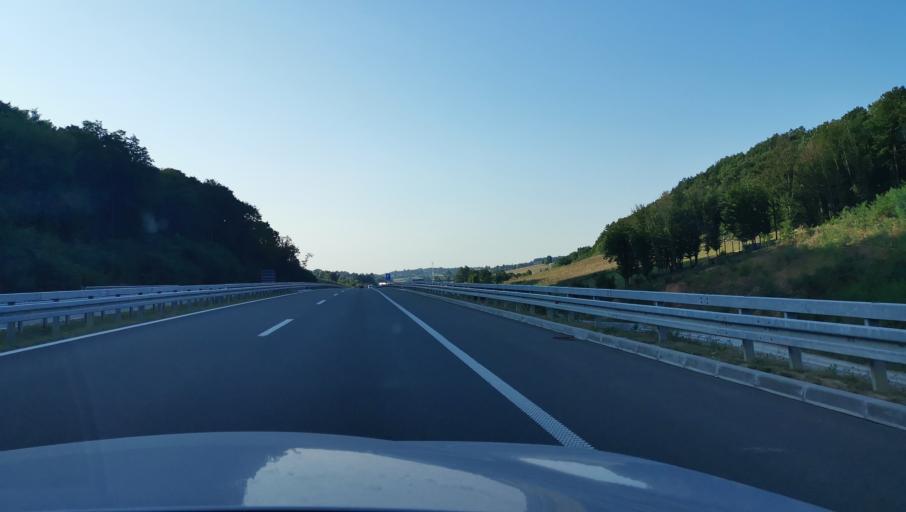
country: RS
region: Central Serbia
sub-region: Moravicki Okrug
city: Gornji Milanovac
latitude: 44.0622
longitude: 20.3807
